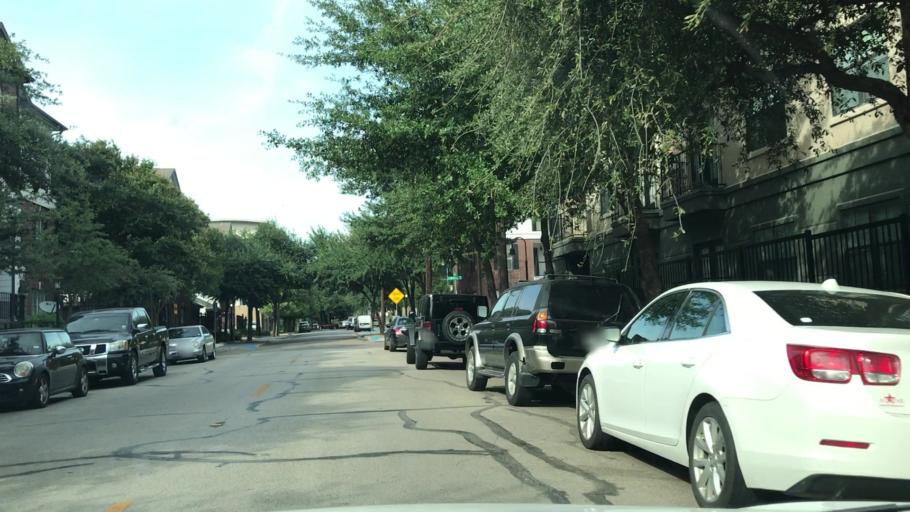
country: US
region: Texas
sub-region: Dallas County
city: Dallas
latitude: 32.7907
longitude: -96.7893
